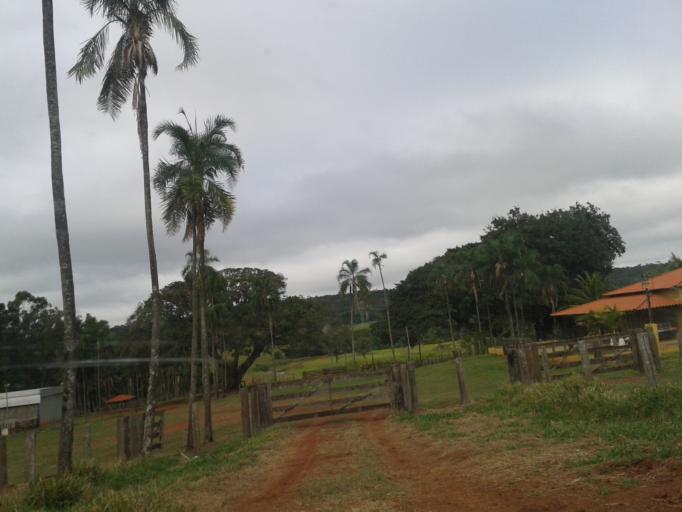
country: BR
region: Minas Gerais
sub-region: Campina Verde
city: Campina Verde
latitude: -19.4266
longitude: -49.6475
